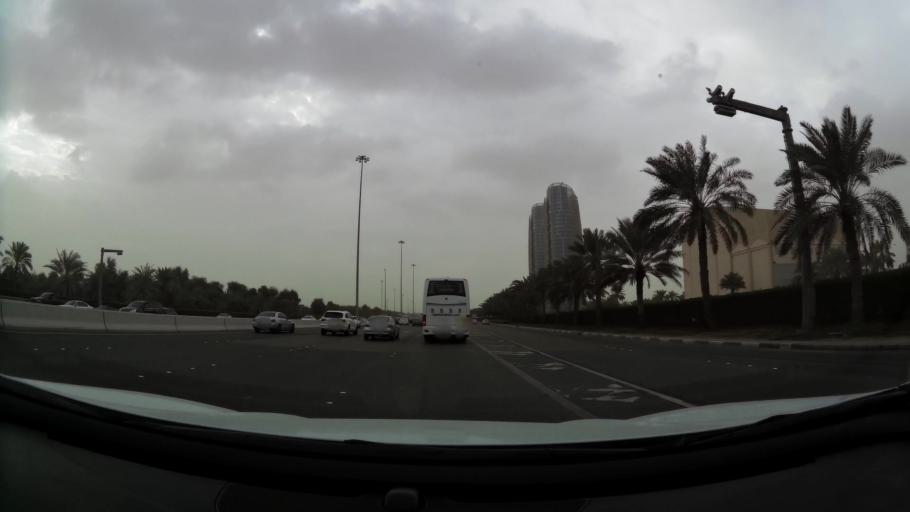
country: AE
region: Abu Dhabi
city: Abu Dhabi
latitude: 24.4606
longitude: 54.3997
